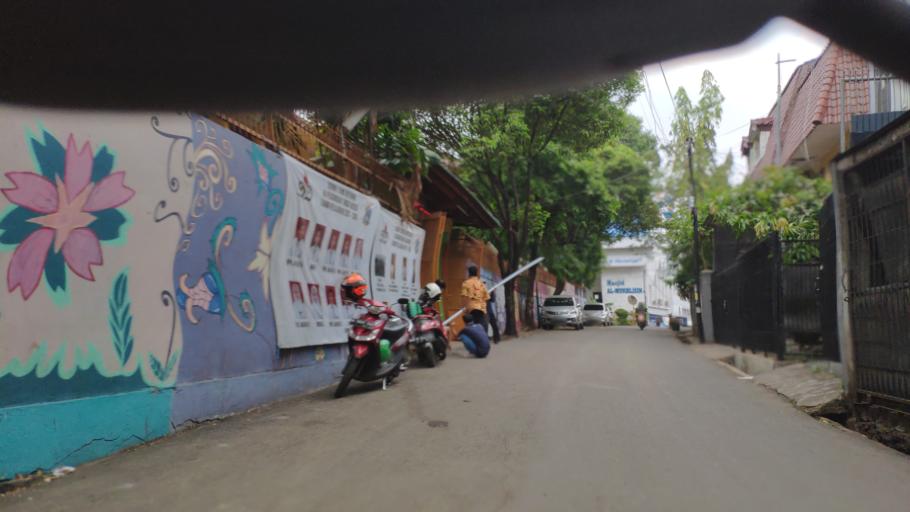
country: ID
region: Jakarta Raya
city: Jakarta
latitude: -6.2689
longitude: 106.7971
